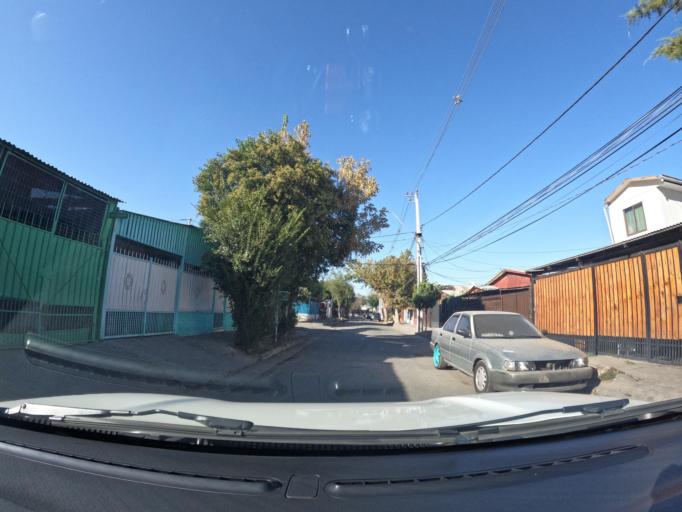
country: CL
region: Santiago Metropolitan
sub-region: Provincia de Santiago
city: Villa Presidente Frei, Nunoa, Santiago, Chile
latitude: -33.5026
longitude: -70.5677
